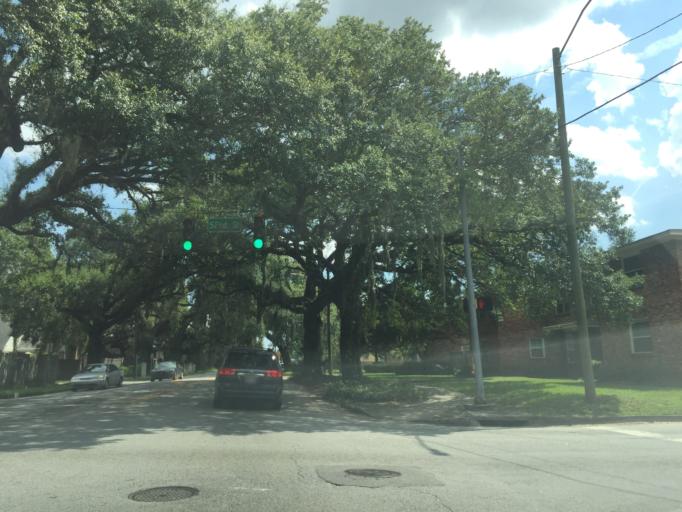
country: US
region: Georgia
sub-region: Chatham County
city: Savannah
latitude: 32.0460
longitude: -81.1046
